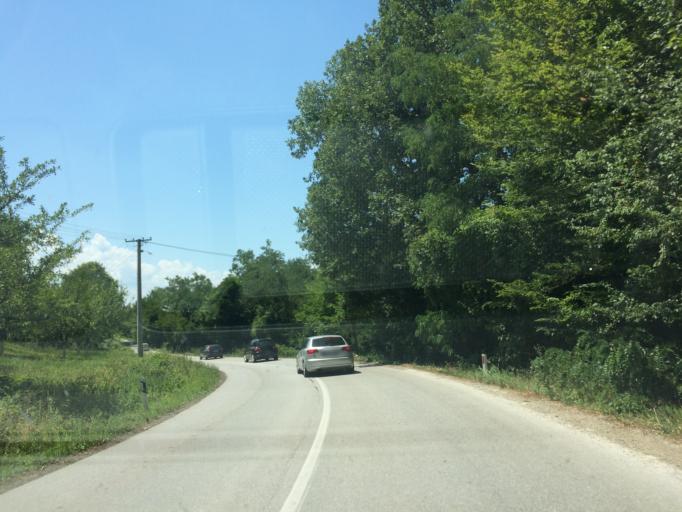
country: RS
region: Central Serbia
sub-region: Kolubarski Okrug
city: Ljig
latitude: 44.2364
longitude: 20.1897
